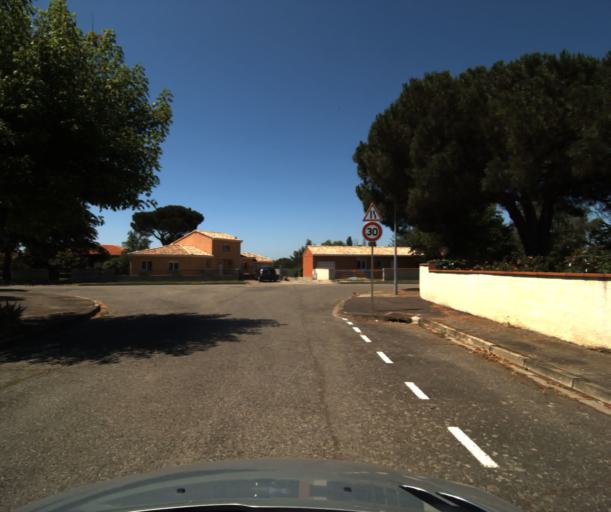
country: FR
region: Midi-Pyrenees
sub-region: Departement de la Haute-Garonne
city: Roquettes
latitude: 43.4934
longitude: 1.3630
